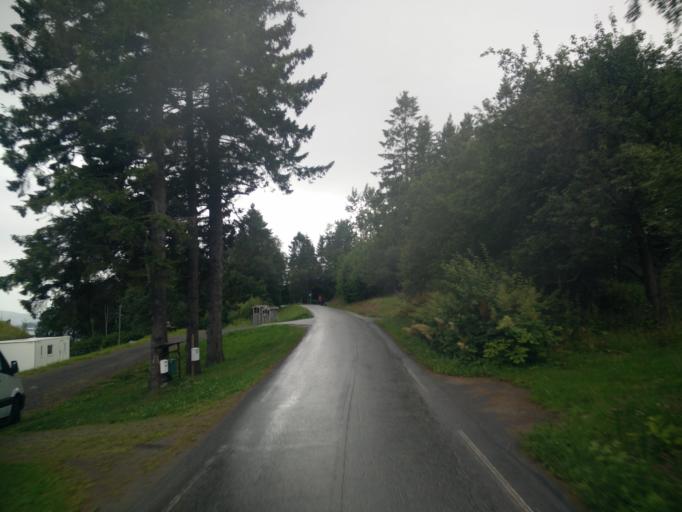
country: NO
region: More og Romsdal
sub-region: Kristiansund
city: Rensvik
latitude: 63.0169
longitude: 7.9048
